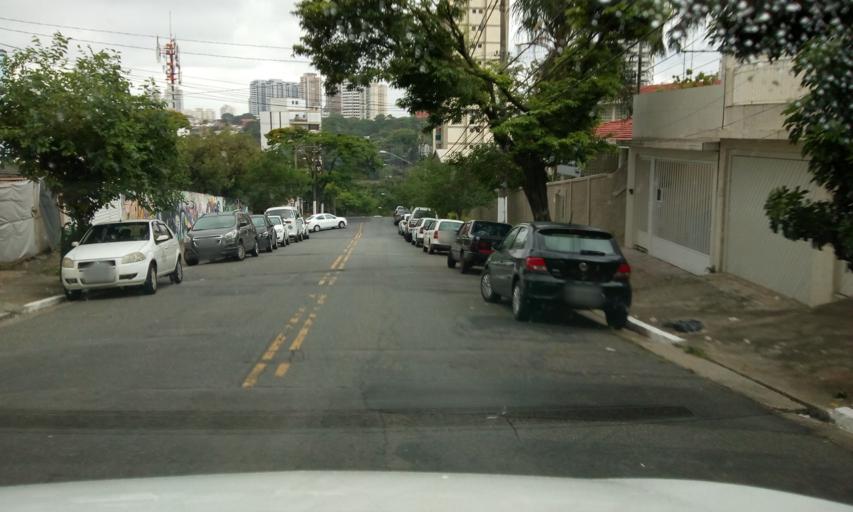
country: BR
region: Sao Paulo
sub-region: Sao Paulo
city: Sao Paulo
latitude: -23.5830
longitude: -46.6313
